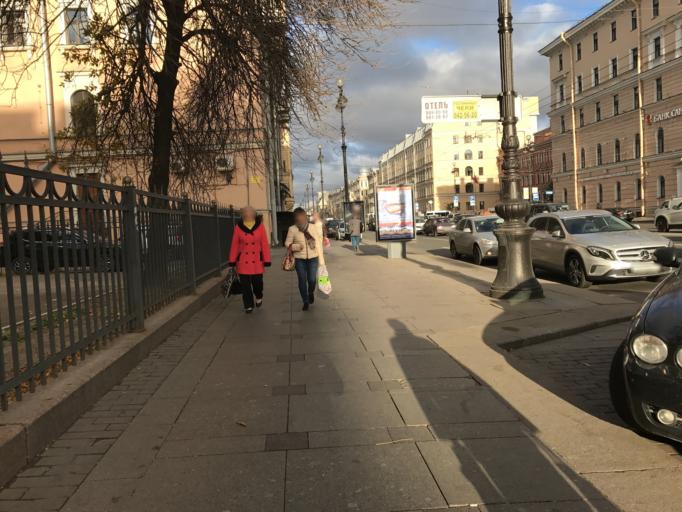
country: RU
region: St.-Petersburg
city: Centralniy
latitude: 59.9247
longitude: 30.3819
